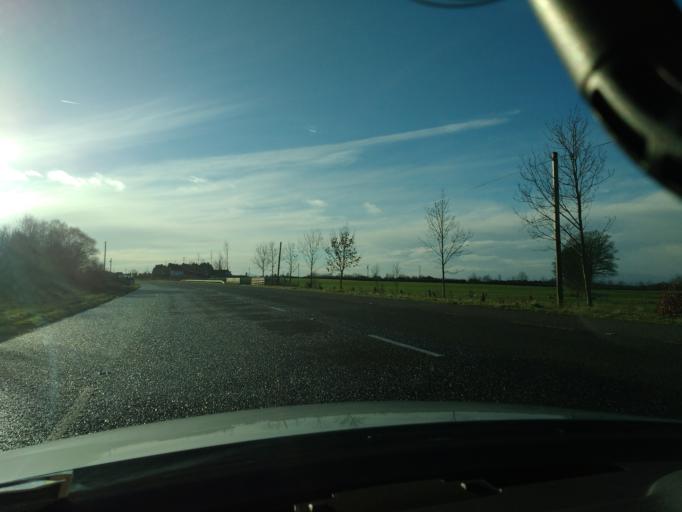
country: IE
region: Munster
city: Thurles
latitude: 52.6875
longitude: -7.6633
